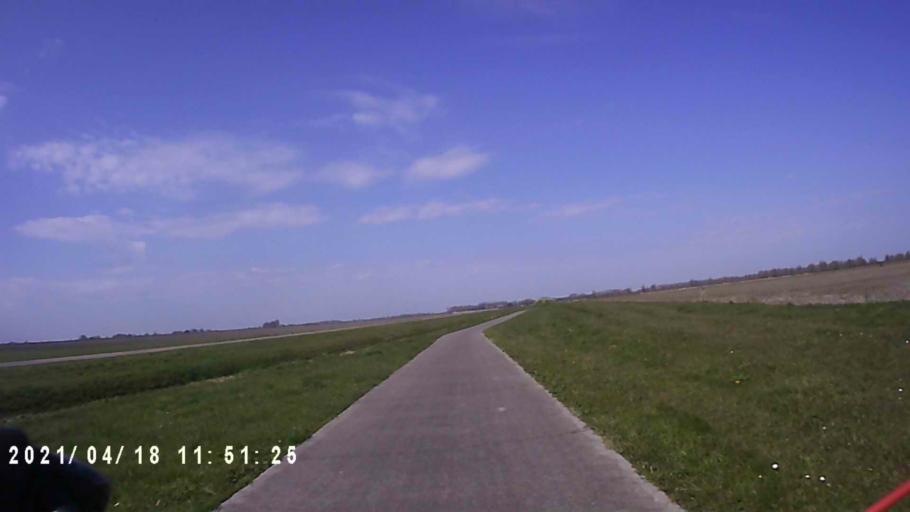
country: NL
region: Friesland
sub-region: Gemeente Kollumerland en Nieuwkruisland
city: Kollum
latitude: 53.3218
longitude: 6.2247
